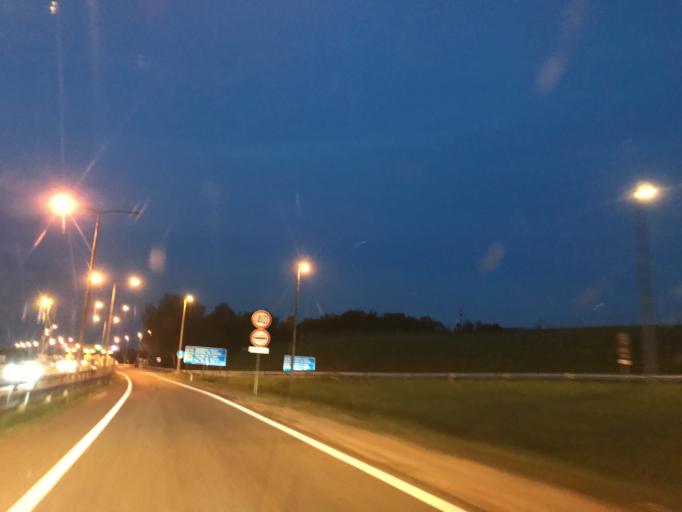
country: RS
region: Central Serbia
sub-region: Podunavski Okrug
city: Smederevo
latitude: 44.5789
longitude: 20.9801
